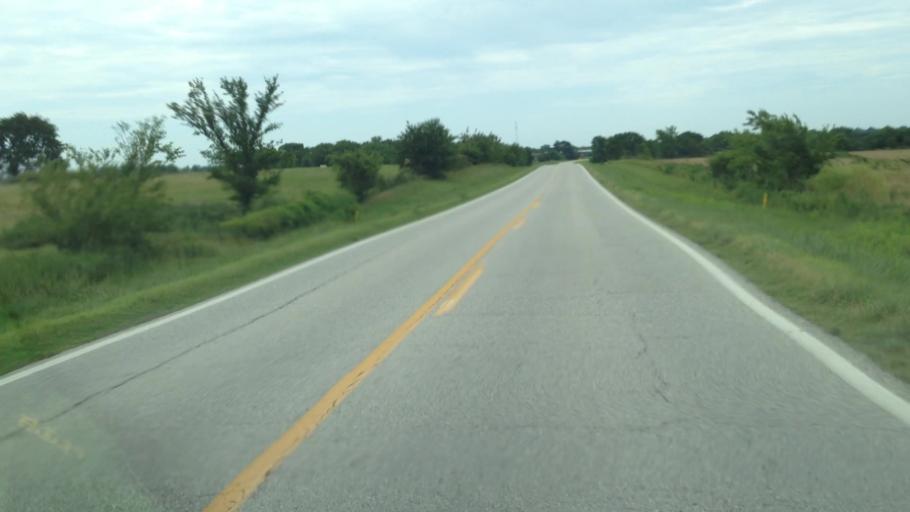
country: US
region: Kansas
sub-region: Labette County
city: Chetopa
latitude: 36.8572
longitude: -95.1159
